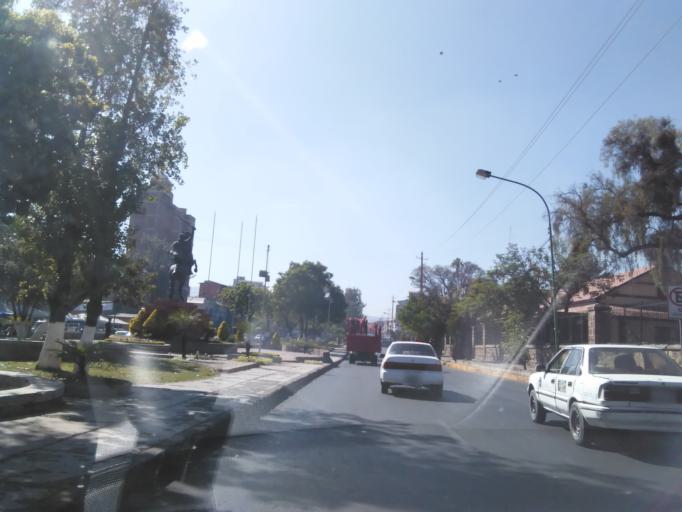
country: BO
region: Cochabamba
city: Cochabamba
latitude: -17.3995
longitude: -66.1600
